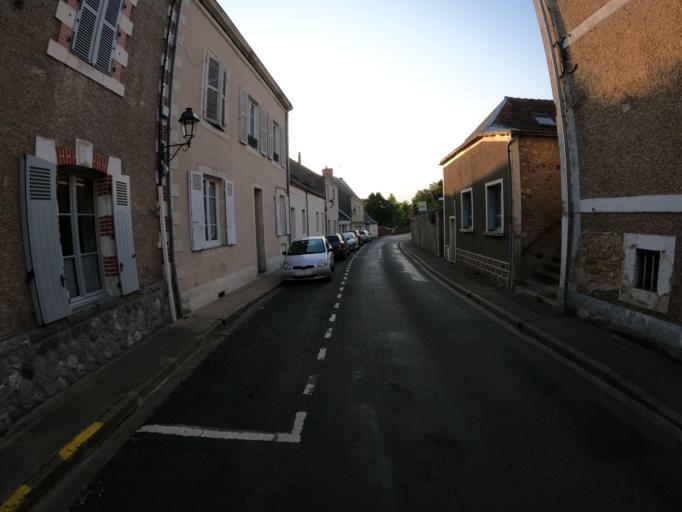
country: FR
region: Pays de la Loire
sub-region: Departement de la Sarthe
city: Parce-sur-Sarthe
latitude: 47.8660
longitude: -0.2072
